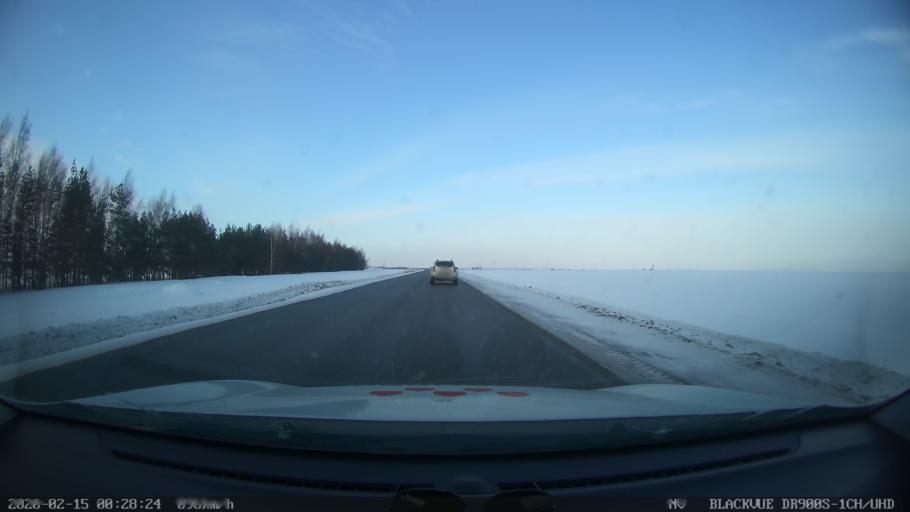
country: RU
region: Tatarstan
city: Verkhniy Uslon
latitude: 55.6419
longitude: 48.8759
